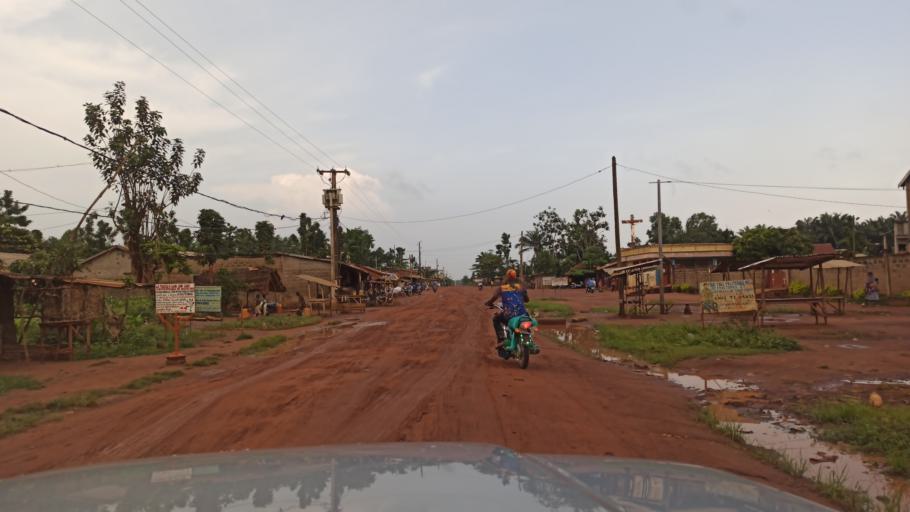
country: BJ
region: Queme
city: Porto-Novo
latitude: 6.4902
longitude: 2.6673
